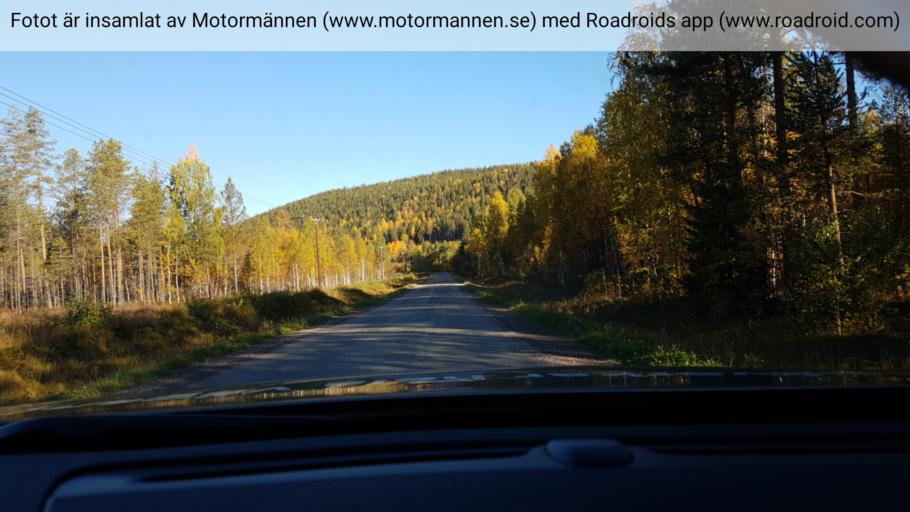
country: SE
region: Norrbotten
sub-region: Alvsbyns Kommun
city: AElvsbyn
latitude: 66.1708
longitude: 21.2431
